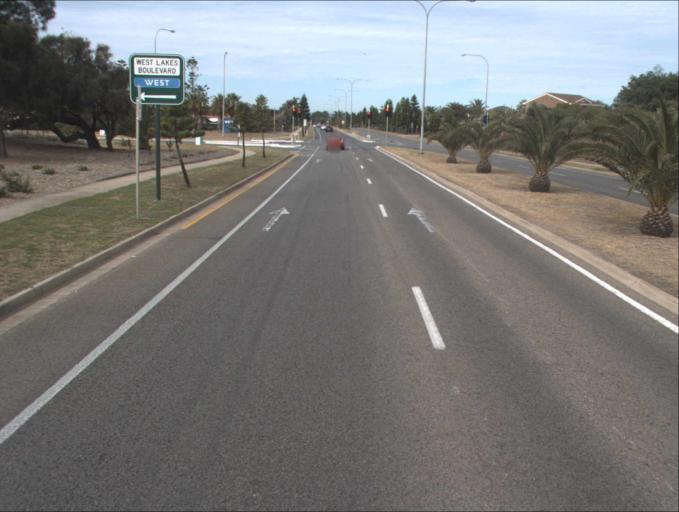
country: AU
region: South Australia
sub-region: Charles Sturt
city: West Lakes Shore
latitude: -34.8708
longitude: 138.4818
